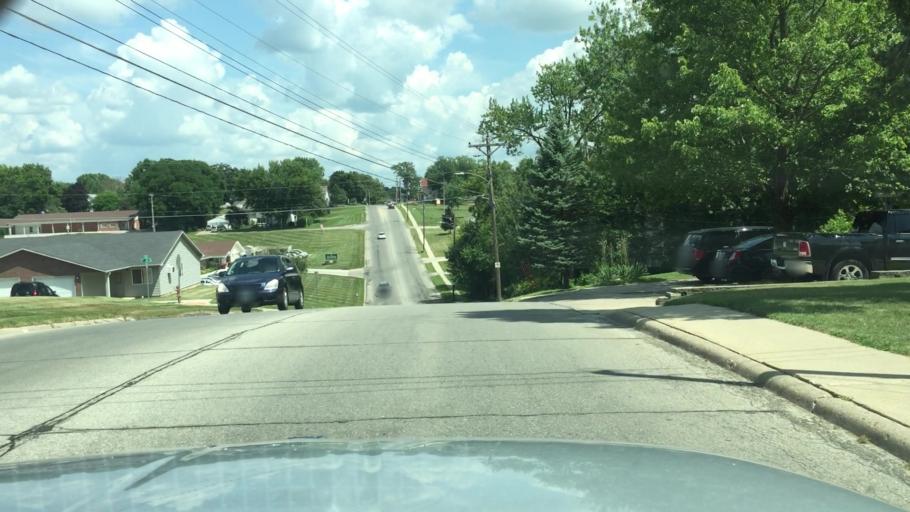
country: US
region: Iowa
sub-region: Jasper County
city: Newton
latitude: 41.6926
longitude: -93.0543
